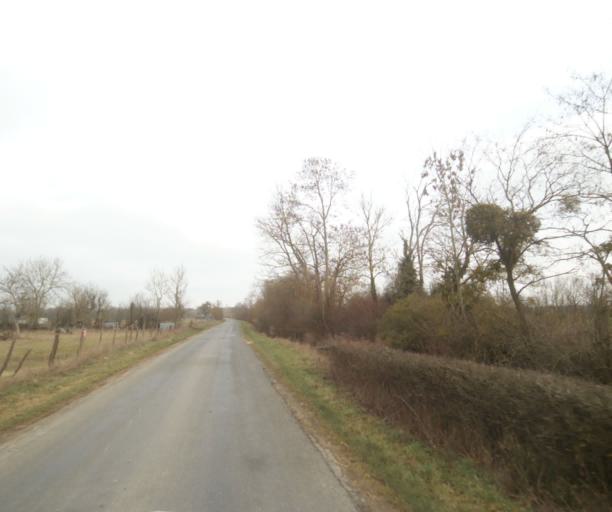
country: FR
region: Champagne-Ardenne
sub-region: Departement de la Haute-Marne
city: Villiers-en-Lieu
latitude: 48.6583
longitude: 4.8277
